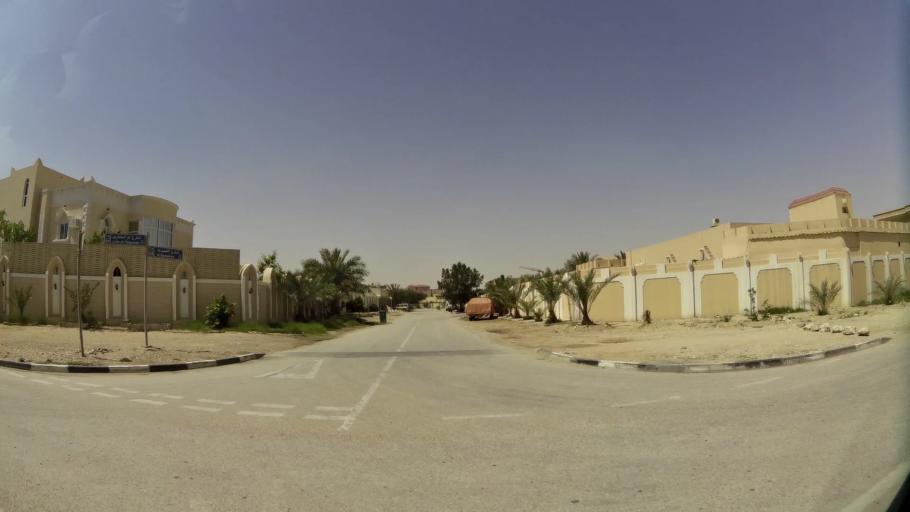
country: QA
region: Baladiyat Umm Salal
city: Umm Salal Muhammad
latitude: 25.3784
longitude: 51.4757
